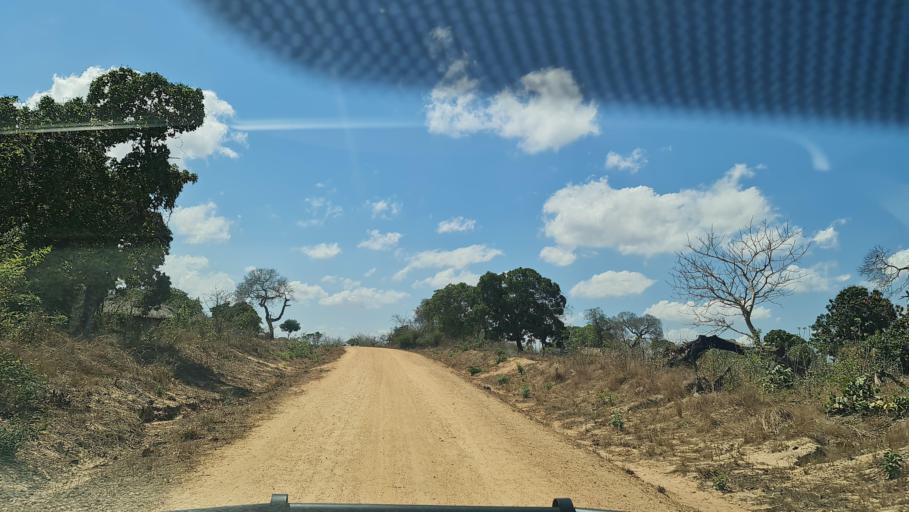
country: MZ
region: Nampula
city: Nacala
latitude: -14.1751
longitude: 40.2063
